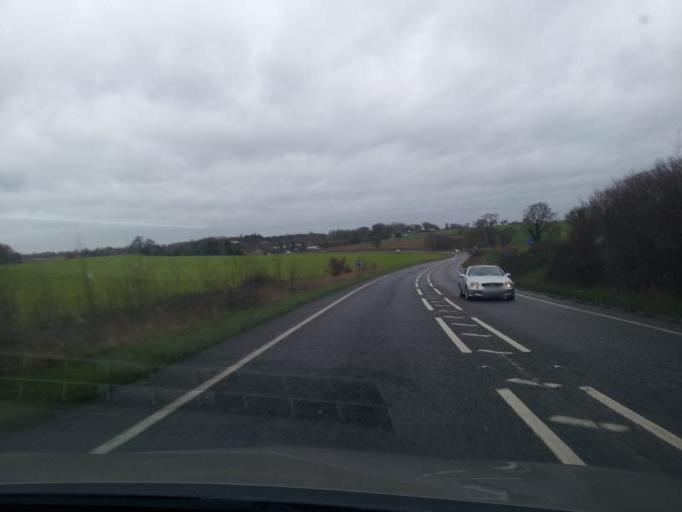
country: GB
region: England
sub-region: Suffolk
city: Botesdale
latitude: 52.3365
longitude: 0.9719
